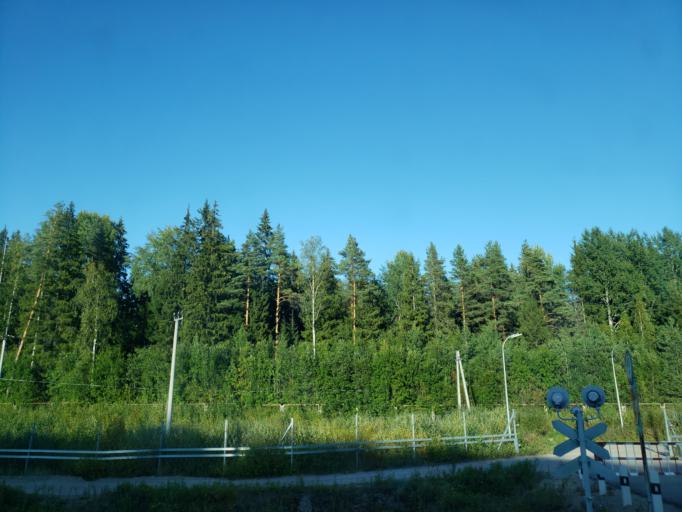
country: FI
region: South Karelia
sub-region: Lappeenranta
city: Nuijamaa
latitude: 60.8459
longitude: 28.3710
